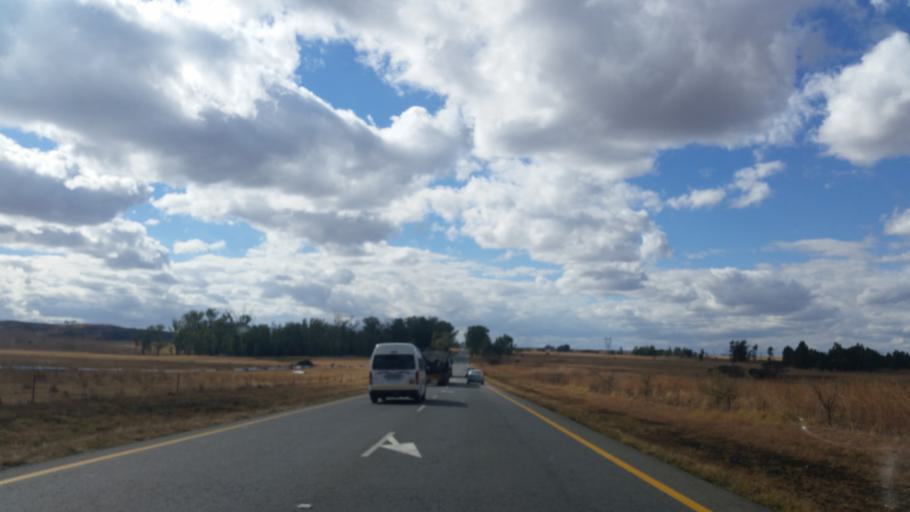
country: ZA
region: KwaZulu-Natal
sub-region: uThukela District Municipality
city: Ladysmith
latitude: -28.4336
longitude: 29.9015
